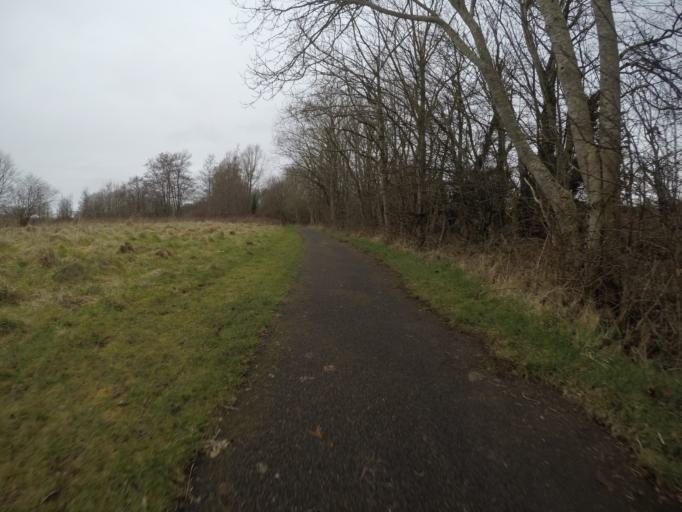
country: GB
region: Scotland
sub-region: North Ayrshire
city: Kilwinning
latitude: 55.6444
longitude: -4.6879
